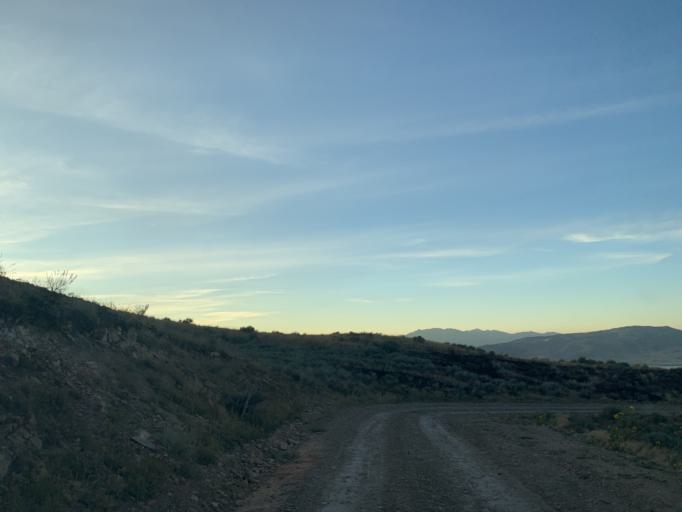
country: US
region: Utah
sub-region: Utah County
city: West Mountain
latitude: 40.0967
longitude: -111.8222
